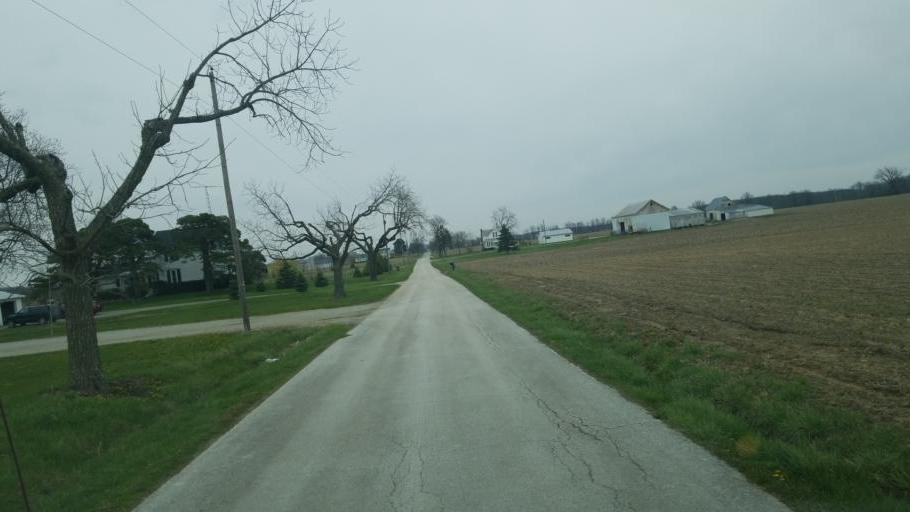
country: US
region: Ohio
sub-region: Hardin County
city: Forest
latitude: 40.7889
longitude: -83.4526
